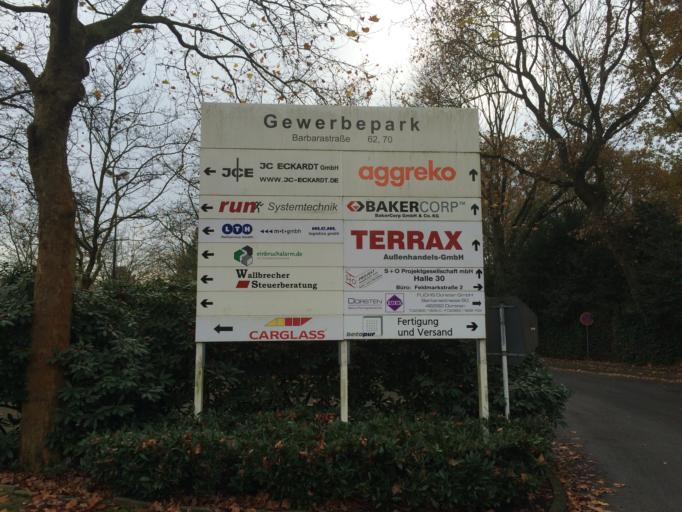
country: DE
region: North Rhine-Westphalia
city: Dorsten
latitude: 51.6512
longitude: 6.9778
